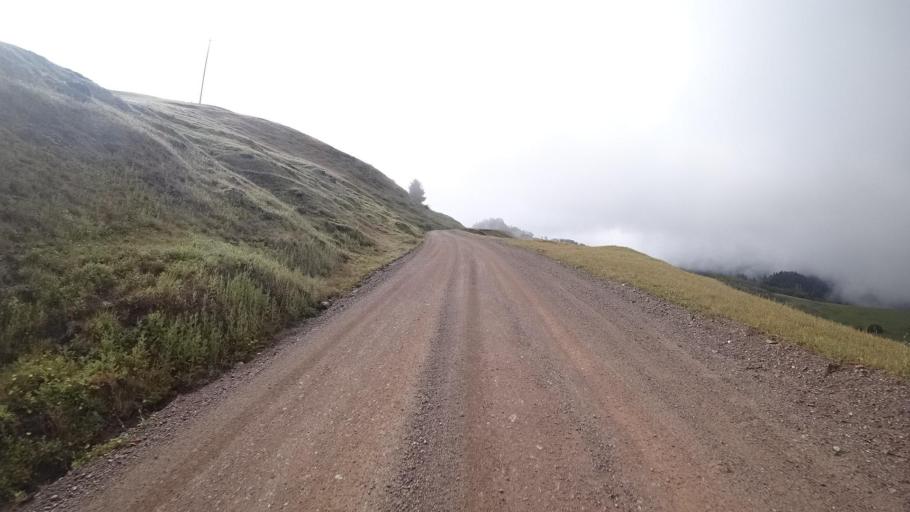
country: US
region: California
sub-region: Humboldt County
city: Redway
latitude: 40.2012
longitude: -123.7117
